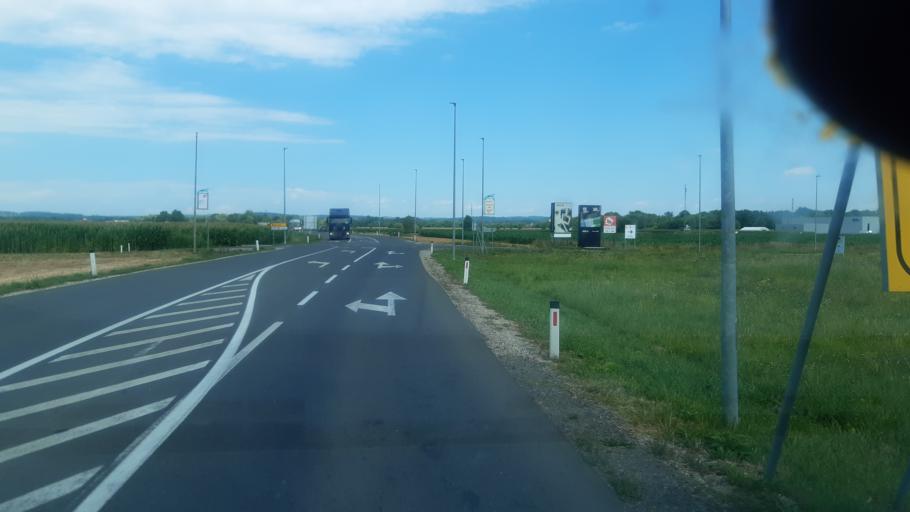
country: SI
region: Murska Sobota
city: Murska Sobota
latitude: 46.6736
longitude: 16.1786
